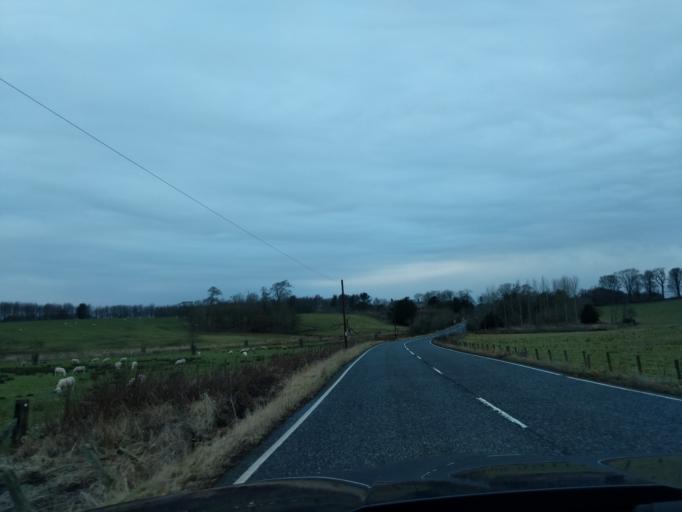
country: GB
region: England
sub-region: Northumberland
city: Rothley
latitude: 55.1413
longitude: -1.9856
